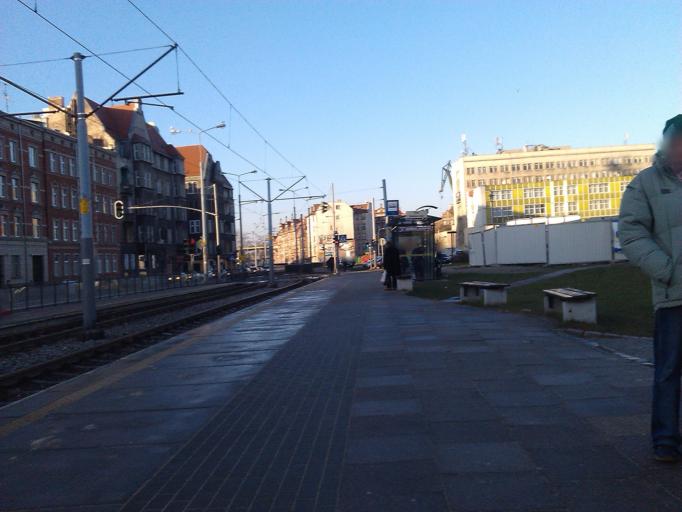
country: PL
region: Pomeranian Voivodeship
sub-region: Gdansk
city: Gdansk
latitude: 54.3604
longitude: 18.6480
